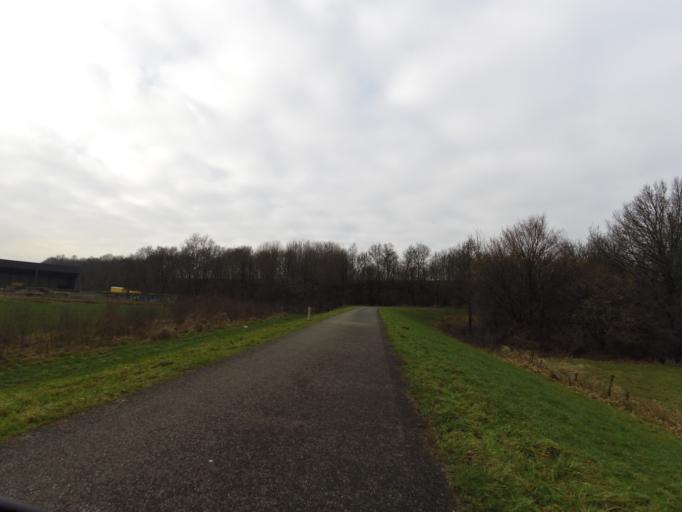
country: NL
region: Gelderland
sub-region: Gemeente Doesburg
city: Doesburg
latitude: 52.0003
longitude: 6.1477
